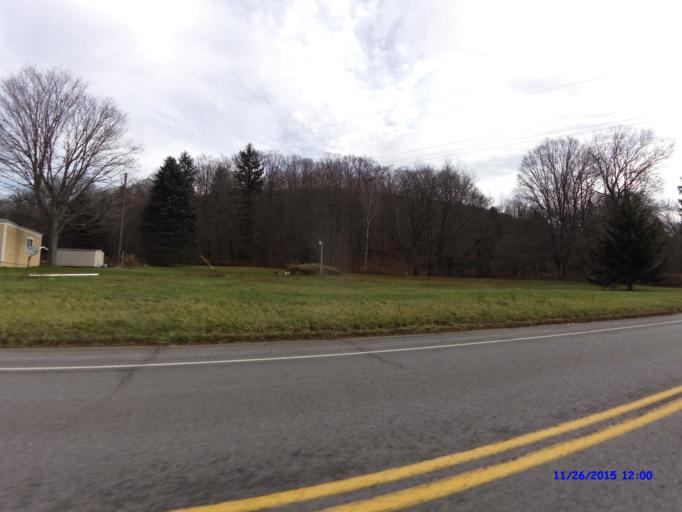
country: US
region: New York
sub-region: Cattaraugus County
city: Franklinville
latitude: 42.2863
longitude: -78.4527
